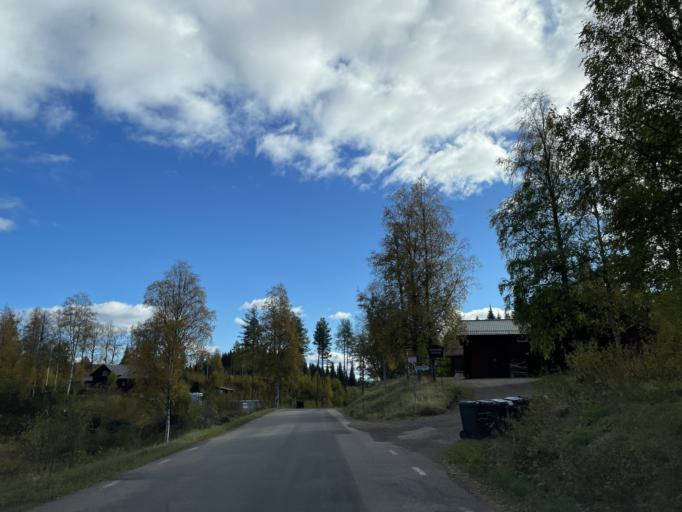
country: SE
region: Dalarna
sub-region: Malung-Saelens kommun
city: Malung
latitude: 61.1203
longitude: 13.2809
